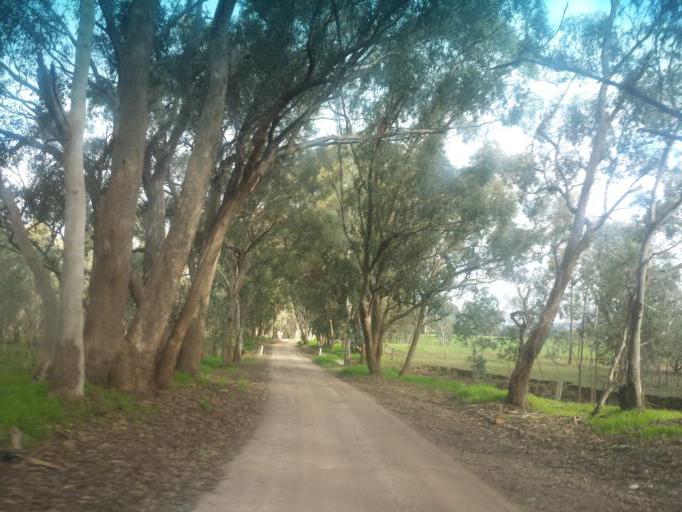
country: AU
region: Victoria
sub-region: Murrindindi
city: Kinglake West
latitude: -37.0396
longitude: 145.2319
